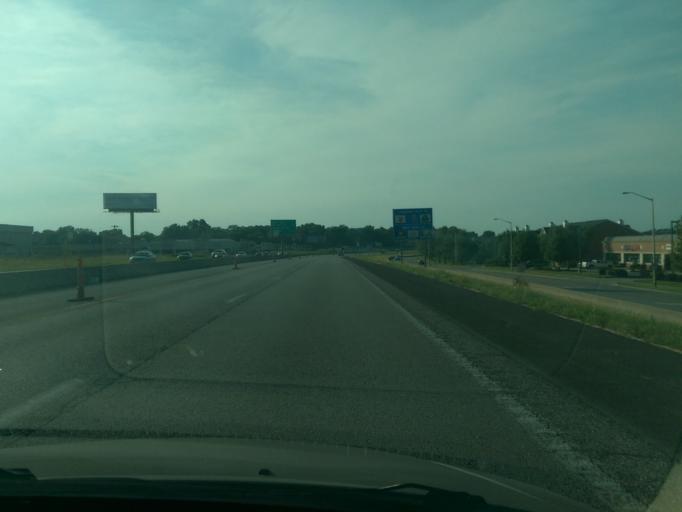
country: US
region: Missouri
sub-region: Platte County
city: Weatherby Lake
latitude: 39.2332
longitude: -94.6553
